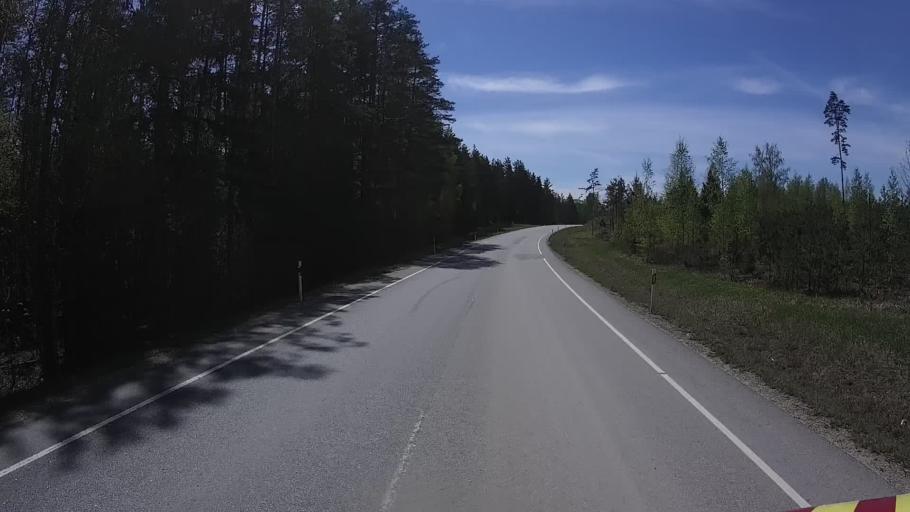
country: EE
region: Polvamaa
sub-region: Polva linn
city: Polva
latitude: 57.9196
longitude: 27.1823
